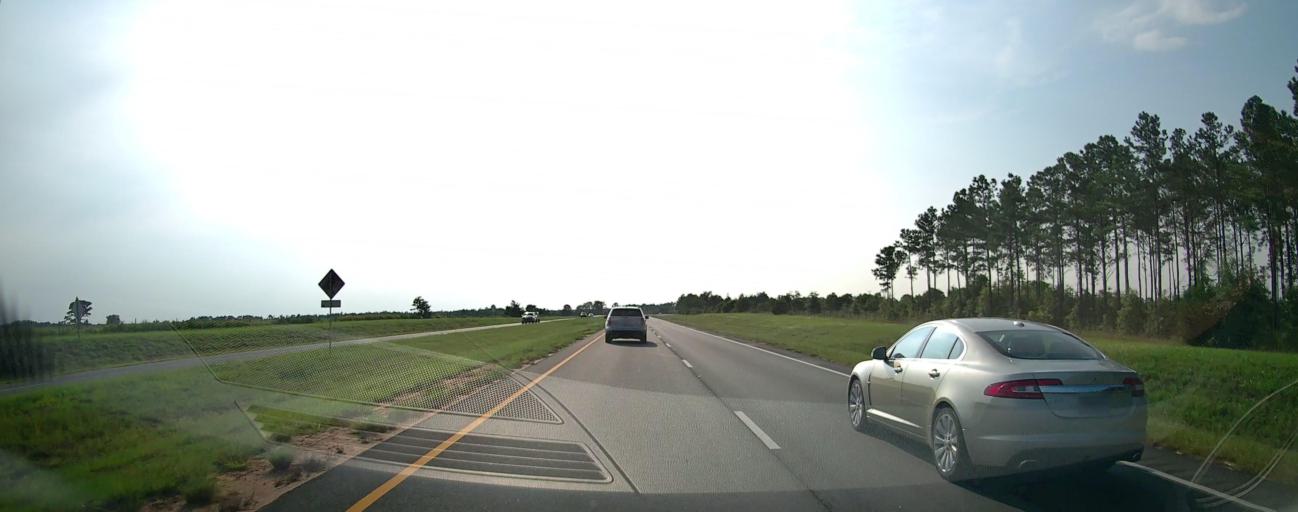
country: US
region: Georgia
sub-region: Taylor County
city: Butler
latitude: 32.5478
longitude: -84.2533
